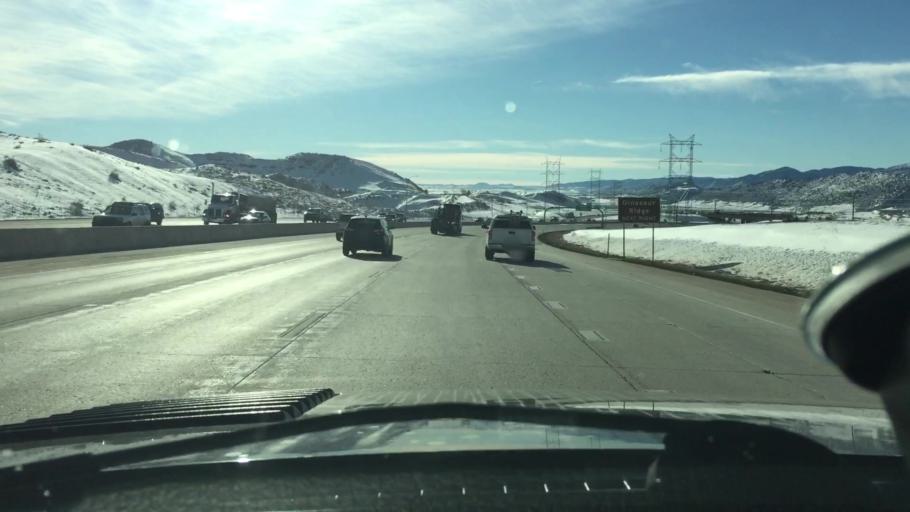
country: US
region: Colorado
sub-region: Jefferson County
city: West Pleasant View
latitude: 39.6939
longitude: -105.1892
